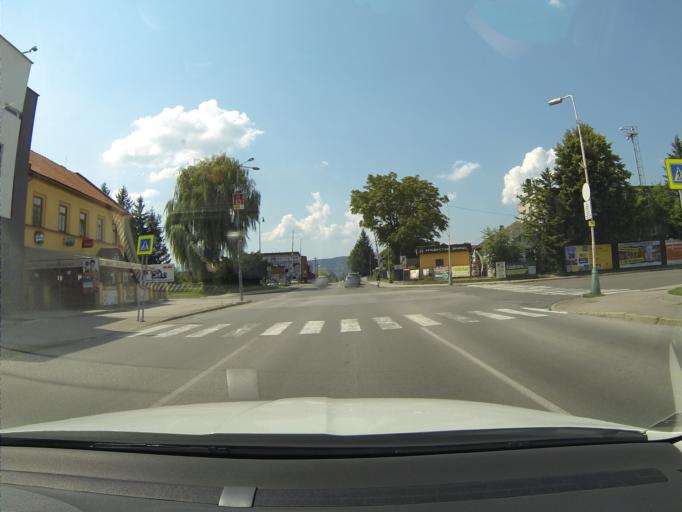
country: SK
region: Nitriansky
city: Prievidza
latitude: 48.7734
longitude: 18.6167
